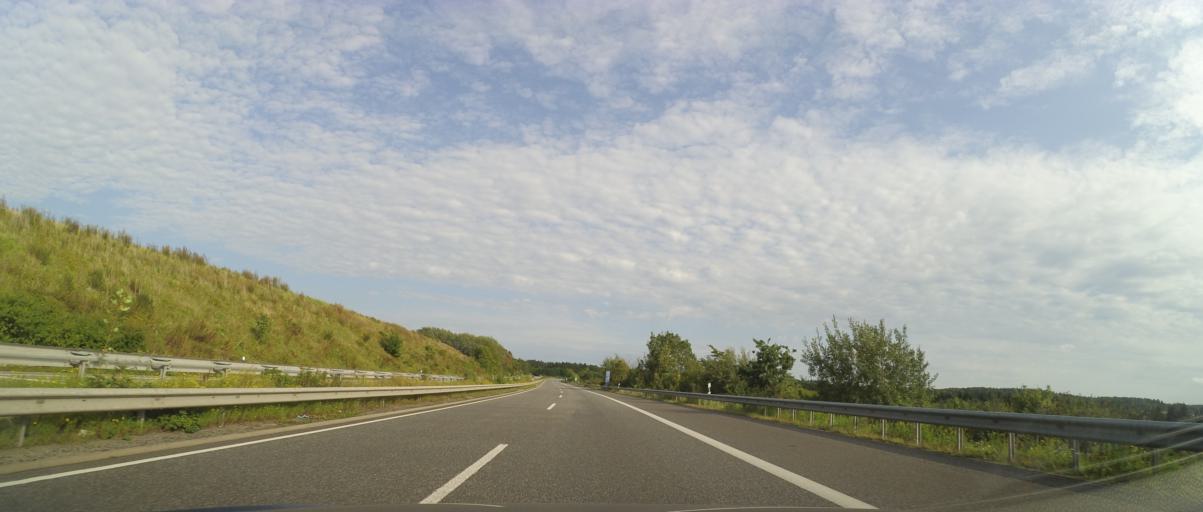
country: DE
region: Rheinland-Pfalz
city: Hasborn
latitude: 50.0495
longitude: 6.9075
